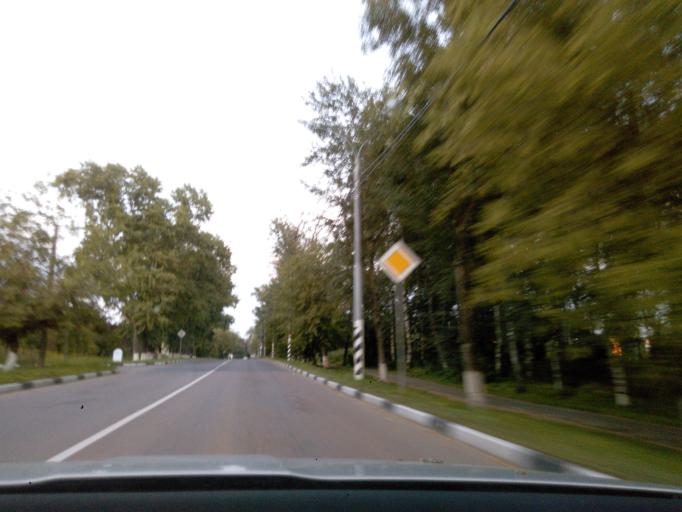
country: RU
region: Moskovskaya
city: Klin
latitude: 56.3396
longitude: 36.7167
